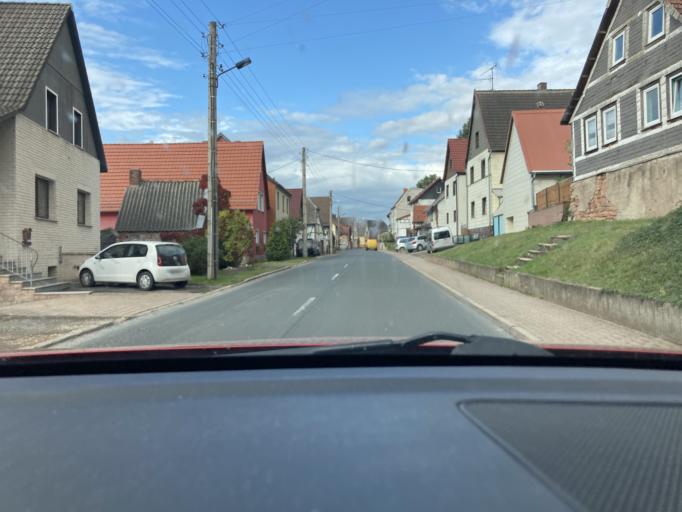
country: DE
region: Thuringia
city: Lipprechterode
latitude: 51.4614
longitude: 10.5539
